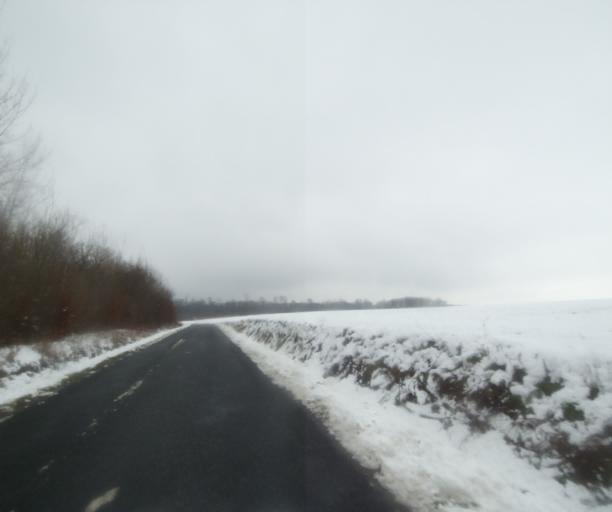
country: FR
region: Champagne-Ardenne
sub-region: Departement de la Haute-Marne
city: Montier-en-Der
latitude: 48.4642
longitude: 4.8205
